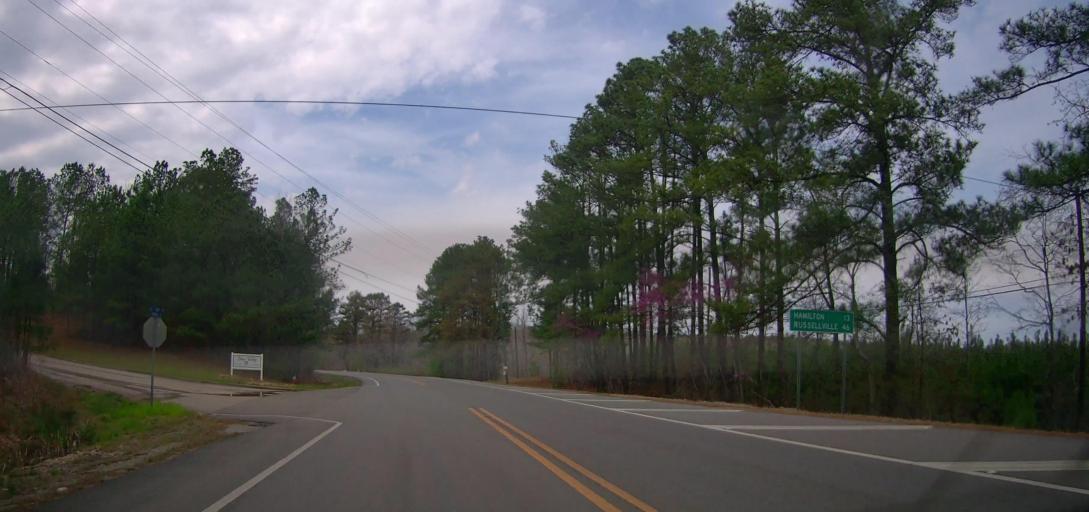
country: US
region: Alabama
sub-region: Marion County
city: Guin
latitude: 33.9835
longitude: -87.9181
